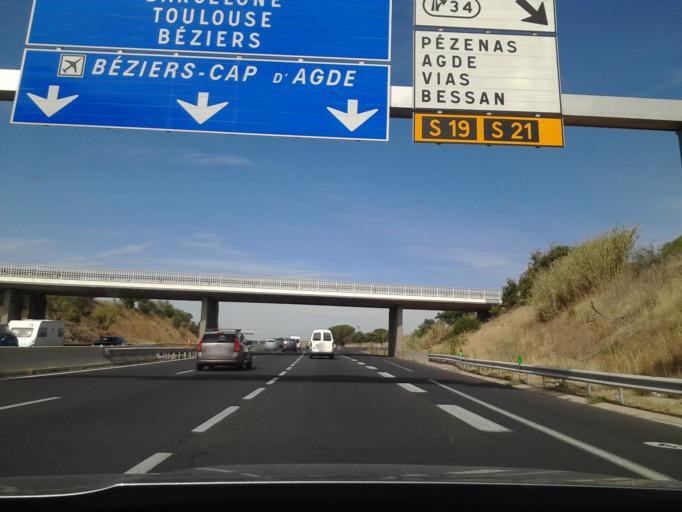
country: FR
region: Languedoc-Roussillon
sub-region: Departement de l'Herault
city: Bessan
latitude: 43.3769
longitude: 3.4166
